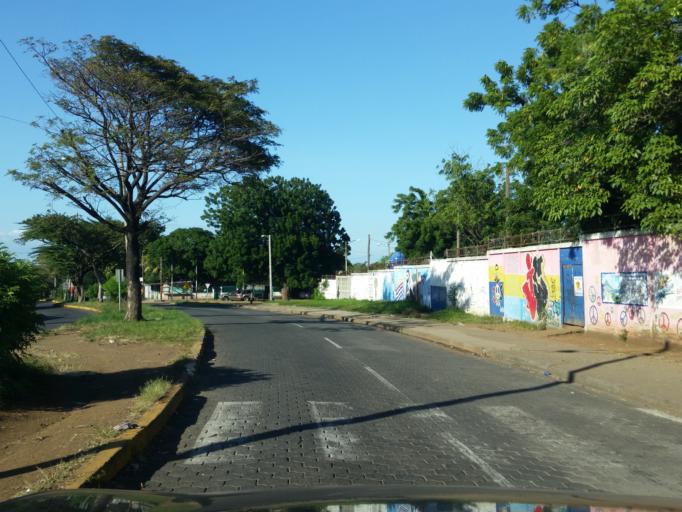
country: NI
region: Managua
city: Managua
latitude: 12.1301
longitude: -86.2905
